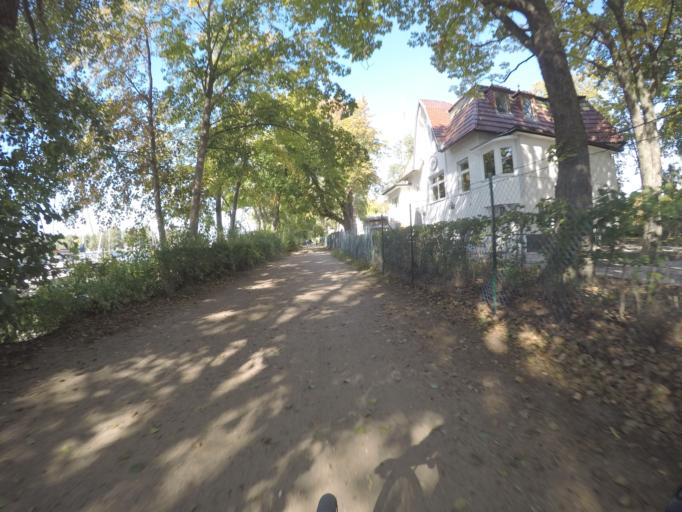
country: DE
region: Berlin
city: Konradshohe
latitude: 52.5719
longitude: 13.2276
